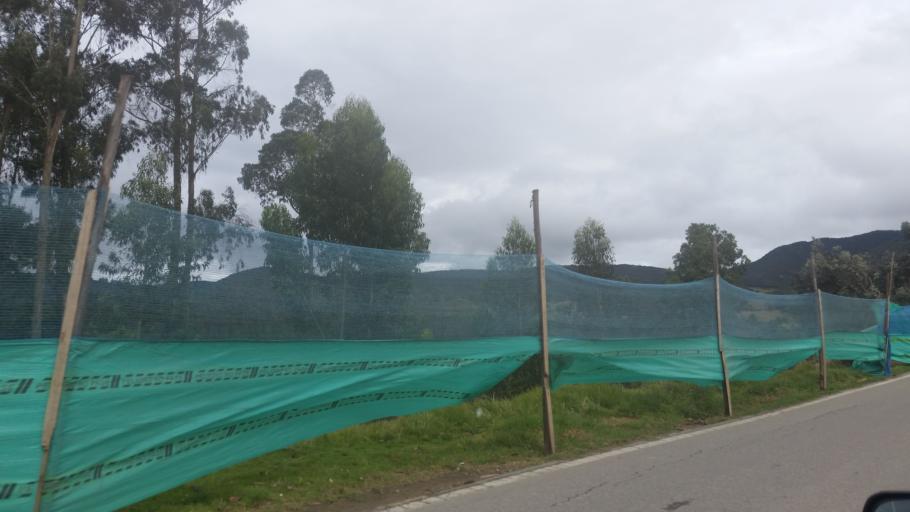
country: CO
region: Cundinamarca
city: La Calera
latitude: 4.7107
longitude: -73.9718
